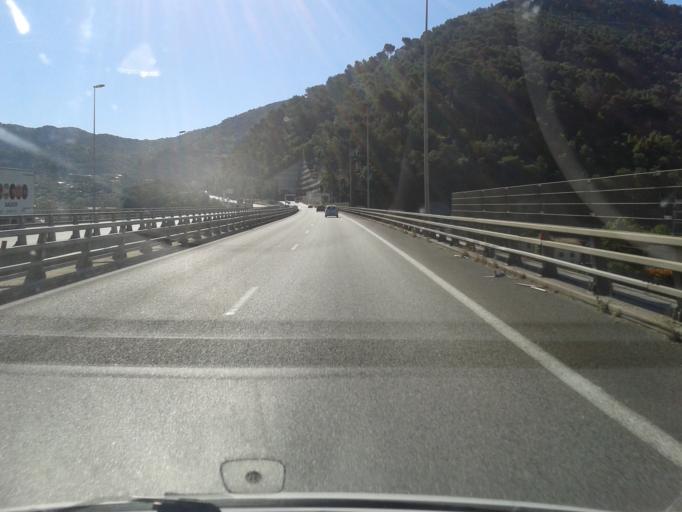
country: FR
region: Provence-Alpes-Cote d'Azur
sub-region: Departement des Alpes-Maritimes
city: Saint-Andre-de-la-Roche
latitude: 43.7333
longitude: 7.2887
